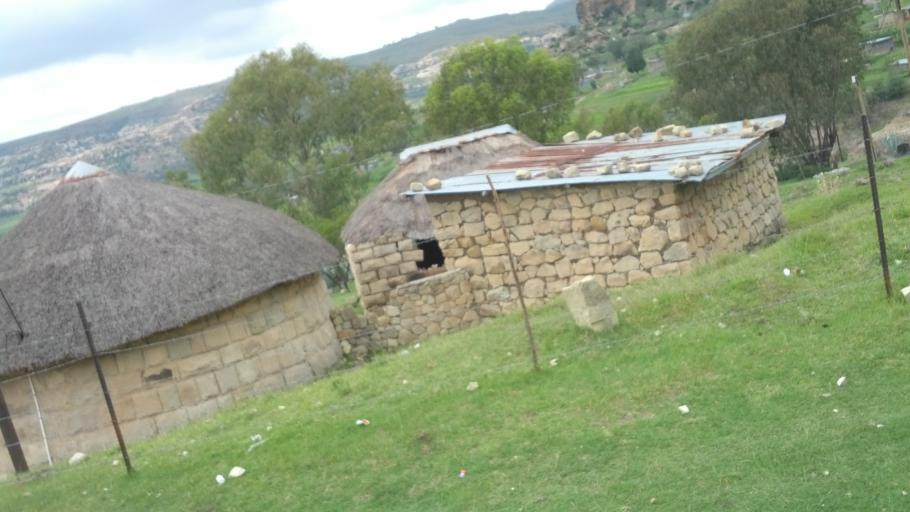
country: LS
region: Leribe
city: Leribe
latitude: -29.0350
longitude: 28.0220
